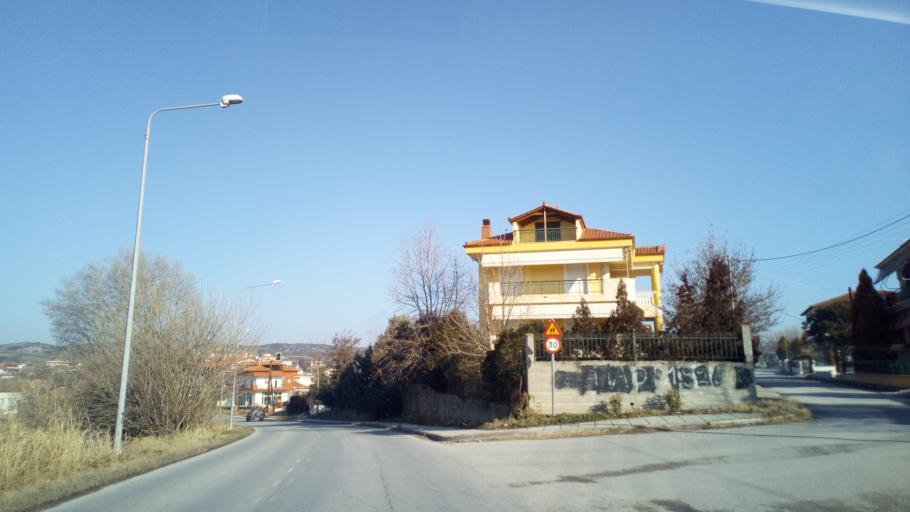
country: GR
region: Central Macedonia
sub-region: Nomos Thessalonikis
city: Kolchikon
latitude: 40.7532
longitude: 23.1319
